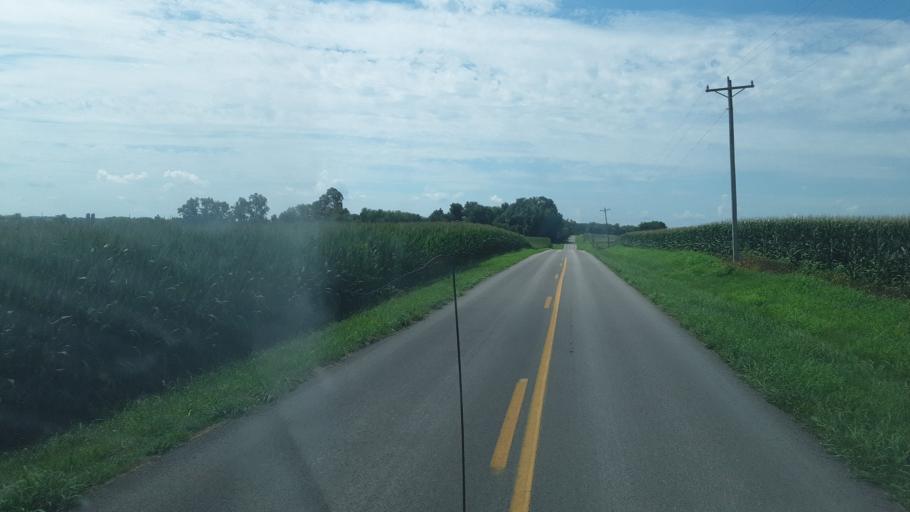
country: US
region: Kentucky
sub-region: Christian County
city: Oak Grove
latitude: 36.7397
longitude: -87.3214
